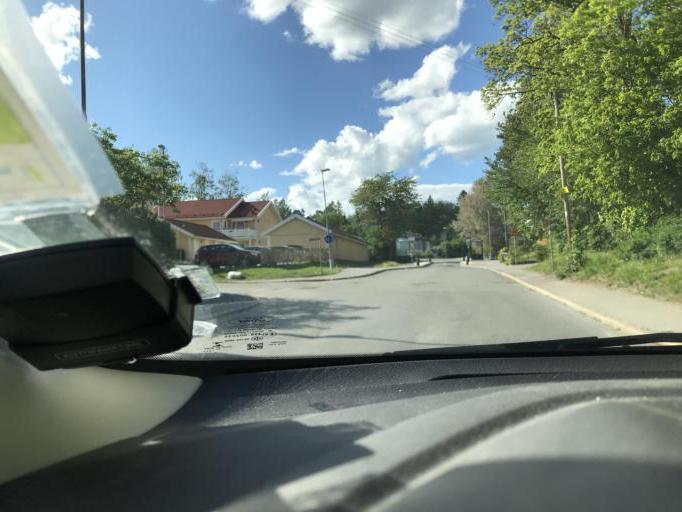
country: SE
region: Stockholm
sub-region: Botkyrka Kommun
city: Tumba
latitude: 59.1971
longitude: 17.8241
